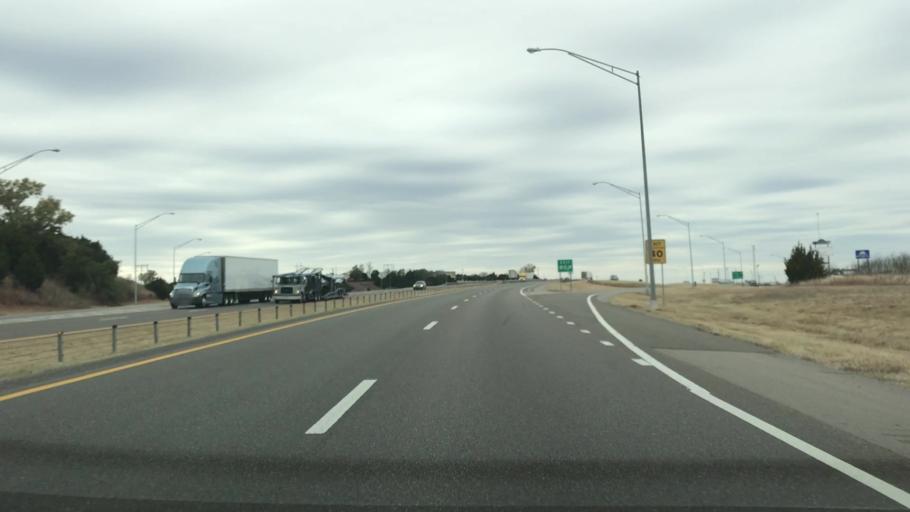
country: US
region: Oklahoma
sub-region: Custer County
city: Weatherford
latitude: 35.5204
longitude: -98.7229
